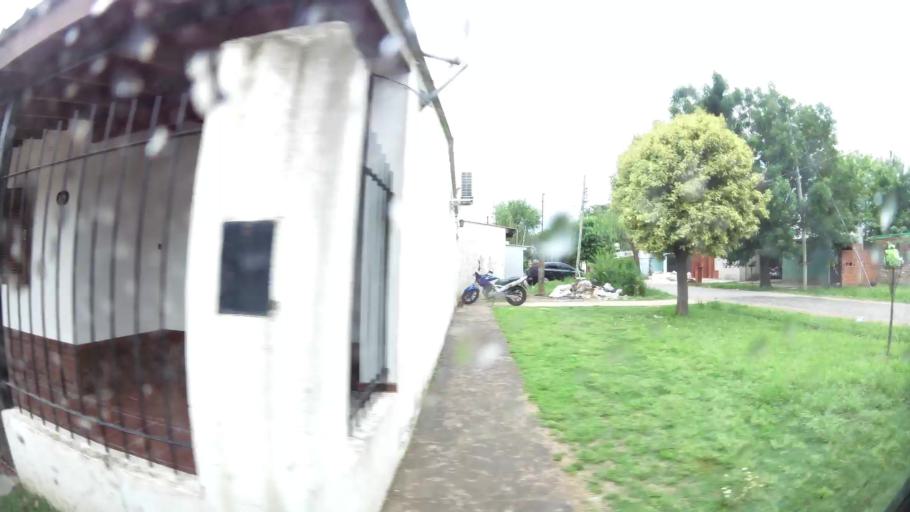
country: AR
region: Buenos Aires
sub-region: Partido de Zarate
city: Zarate
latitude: -34.1136
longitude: -59.0421
